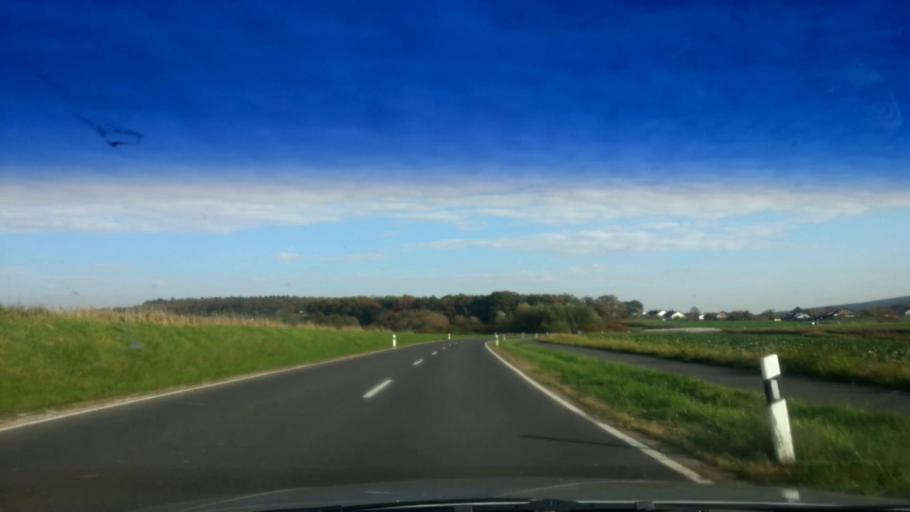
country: DE
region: Bavaria
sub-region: Upper Franconia
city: Stegaurach
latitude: 49.8552
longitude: 10.8684
